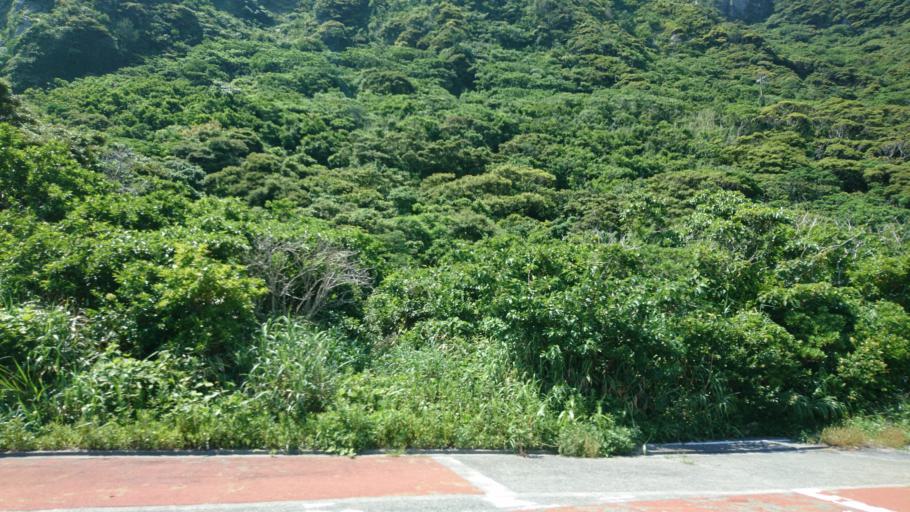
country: JP
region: Shizuoka
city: Shimoda
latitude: 34.3918
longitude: 139.2774
